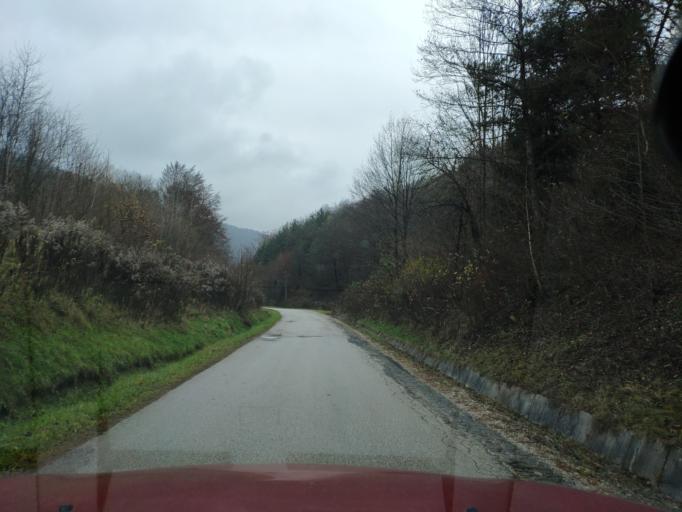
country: SK
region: Kosicky
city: Roznava
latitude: 48.7039
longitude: 20.5449
